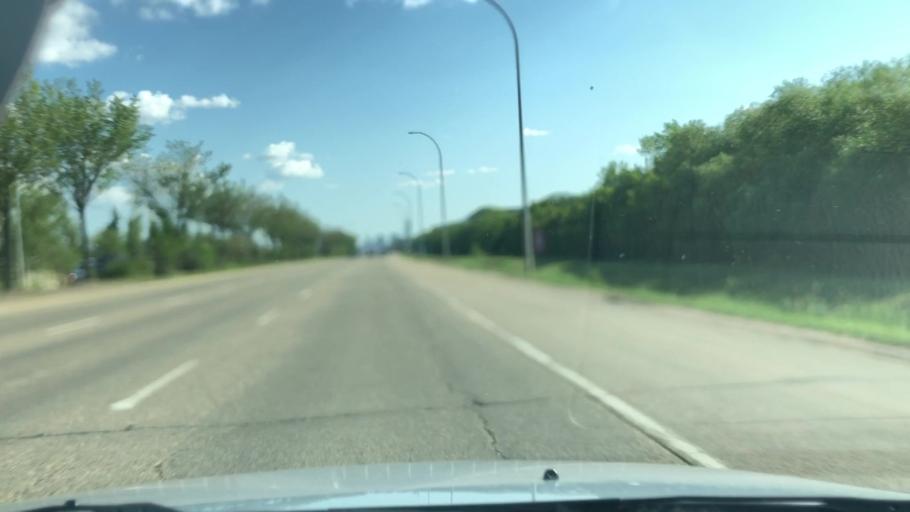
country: CA
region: Alberta
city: Edmonton
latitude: 53.6059
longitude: -113.4920
